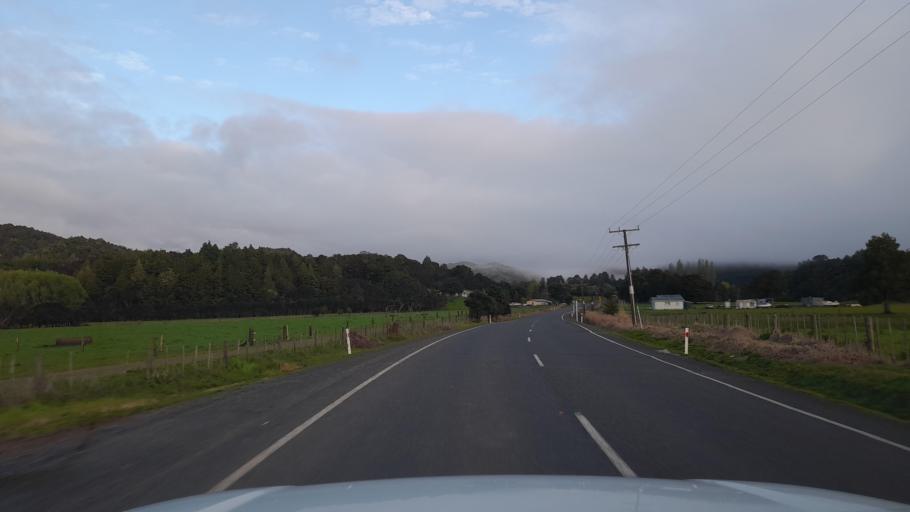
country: NZ
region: Northland
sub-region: Kaipara District
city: Dargaville
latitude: -35.6443
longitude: 173.8603
